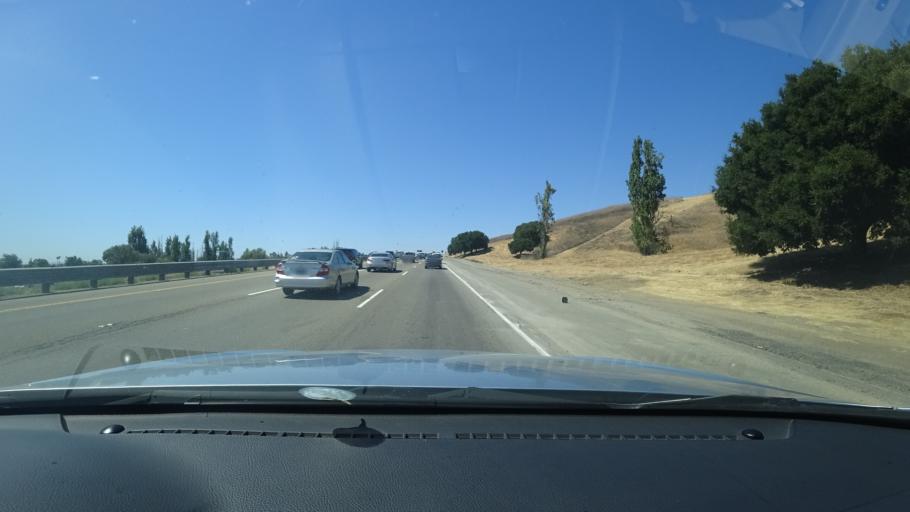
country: US
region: California
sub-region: Santa Clara County
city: Milpitas
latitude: 37.4759
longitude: -121.9111
